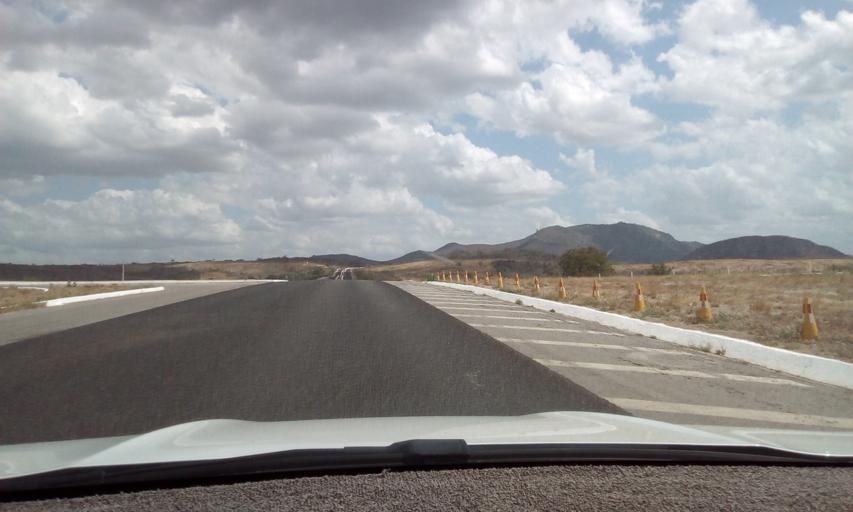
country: BR
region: Pernambuco
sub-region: Toritama
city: Toritama
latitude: -8.0545
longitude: -36.0489
